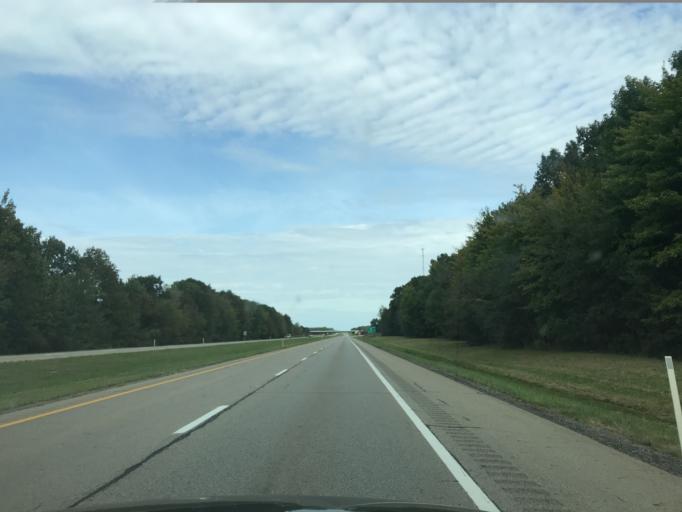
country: US
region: Ohio
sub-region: Ashtabula County
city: Roaming Shores
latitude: 41.5990
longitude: -80.7132
